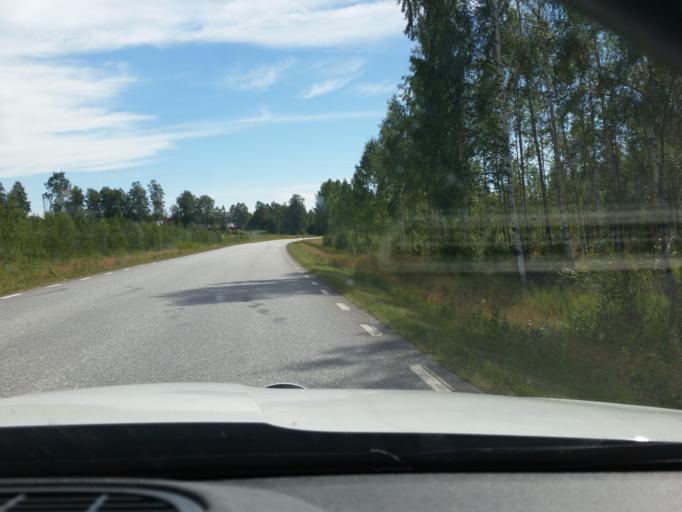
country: SE
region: Norrbotten
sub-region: Pitea Kommun
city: Norrfjarden
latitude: 65.4345
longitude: 21.4829
